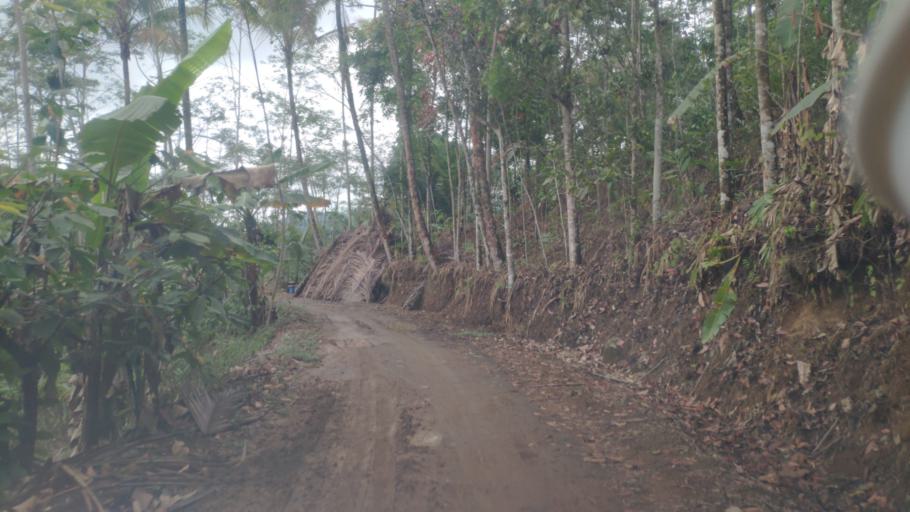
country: ID
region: Central Java
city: Purbalingga
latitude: -7.3057
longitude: 109.5772
